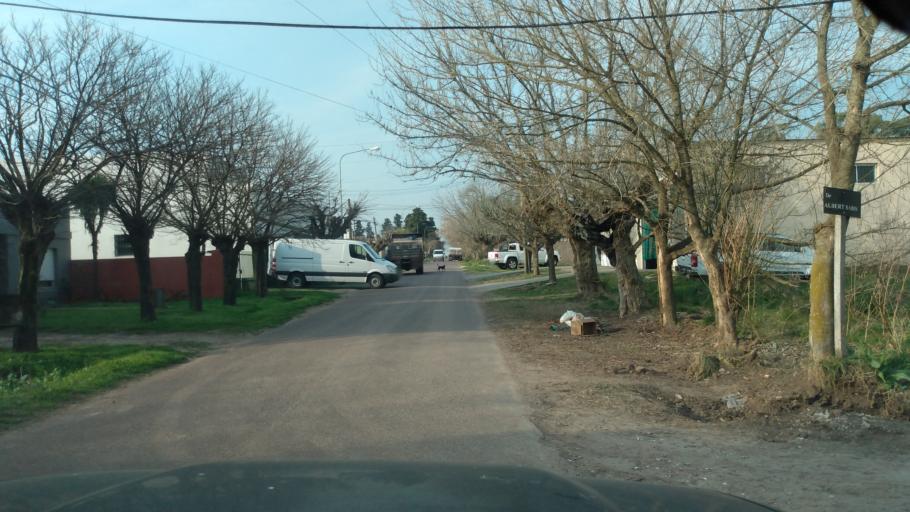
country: AR
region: Buenos Aires
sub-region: Partido de Lujan
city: Lujan
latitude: -34.5777
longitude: -59.1807
